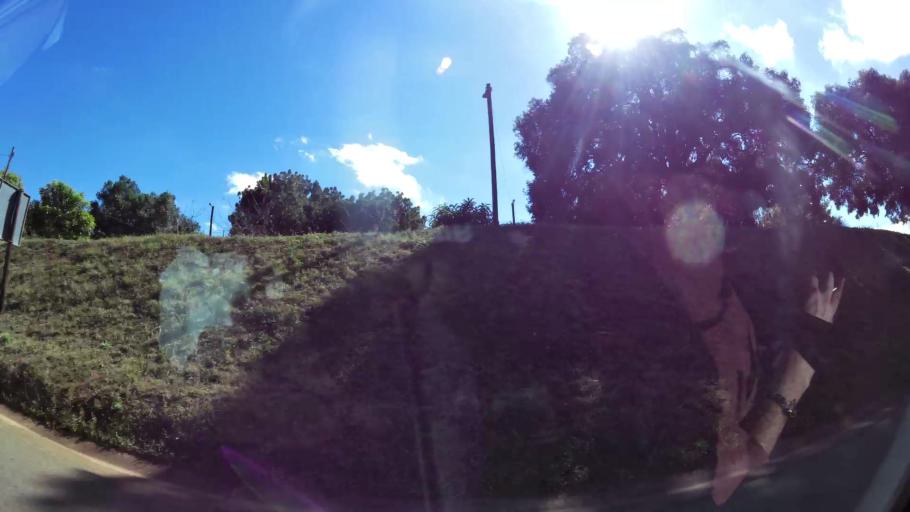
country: ZA
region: Limpopo
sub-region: Mopani District Municipality
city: Tzaneen
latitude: -23.8201
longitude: 30.1652
